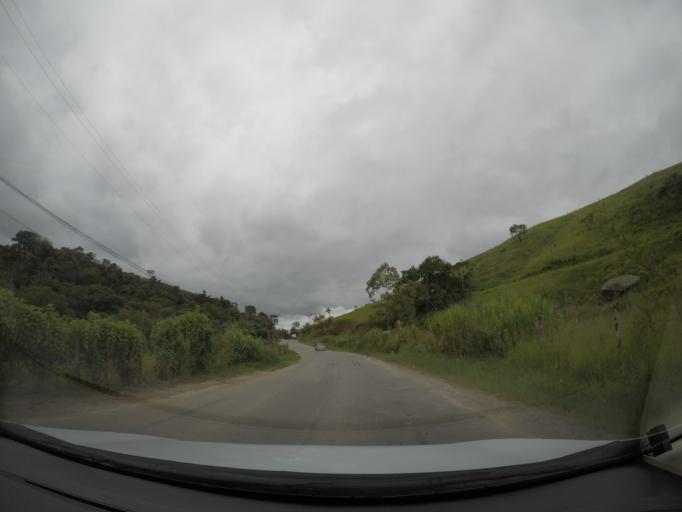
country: BR
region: Sao Paulo
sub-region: Aruja
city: Aruja
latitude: -23.3714
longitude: -46.2970
